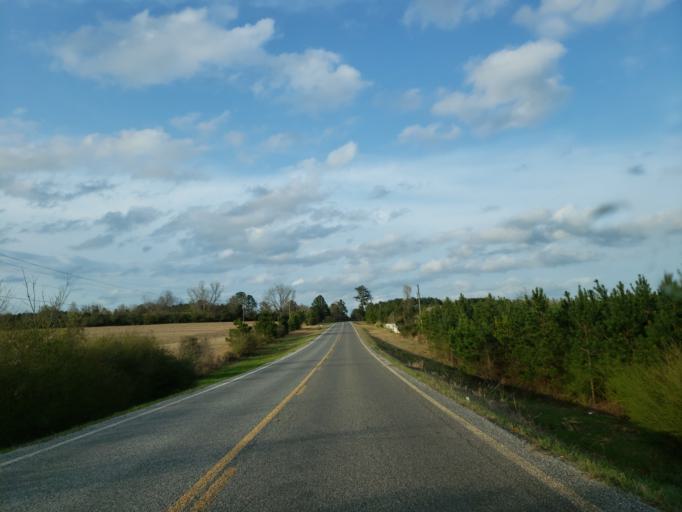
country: US
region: Mississippi
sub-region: Clarke County
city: Stonewall
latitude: 32.1763
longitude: -88.6784
